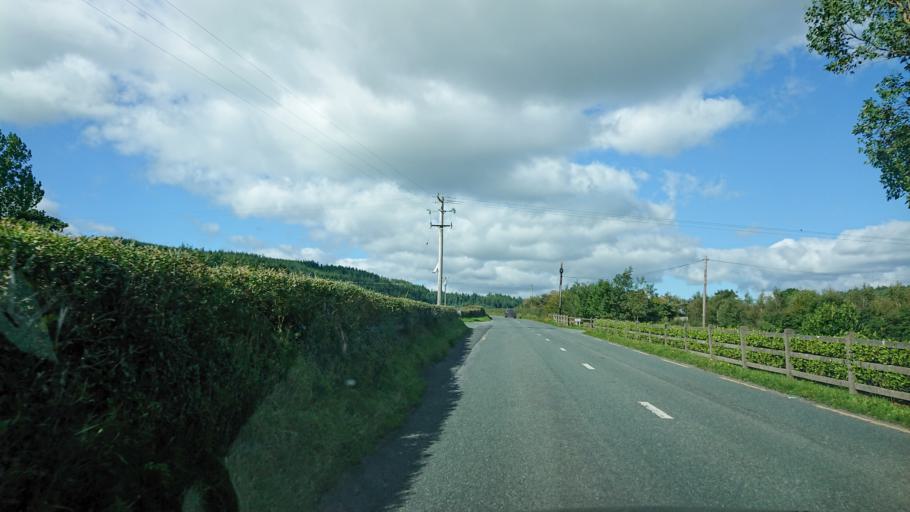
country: IE
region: Munster
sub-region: Waterford
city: Dungarvan
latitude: 52.1160
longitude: -7.6821
